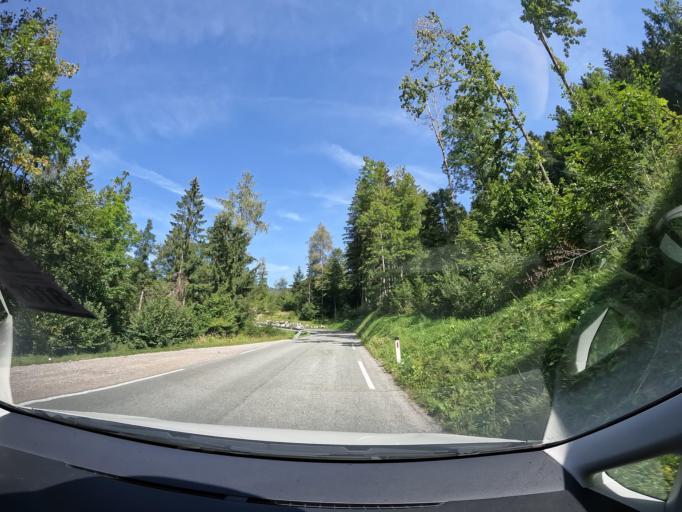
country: AT
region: Carinthia
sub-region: Politischer Bezirk Villach Land
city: Sankt Jakob
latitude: 46.5729
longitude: 14.0789
